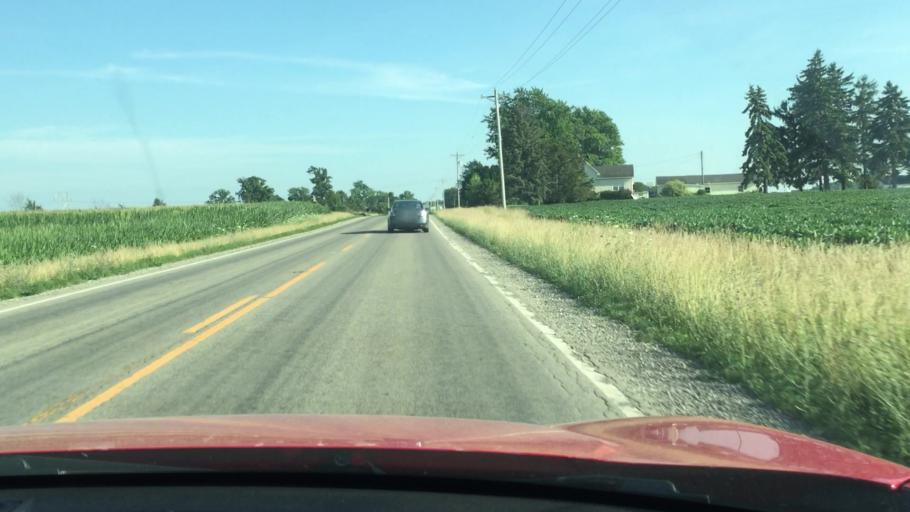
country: US
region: Ohio
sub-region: Hardin County
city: Ada
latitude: 40.6716
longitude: -83.8553
